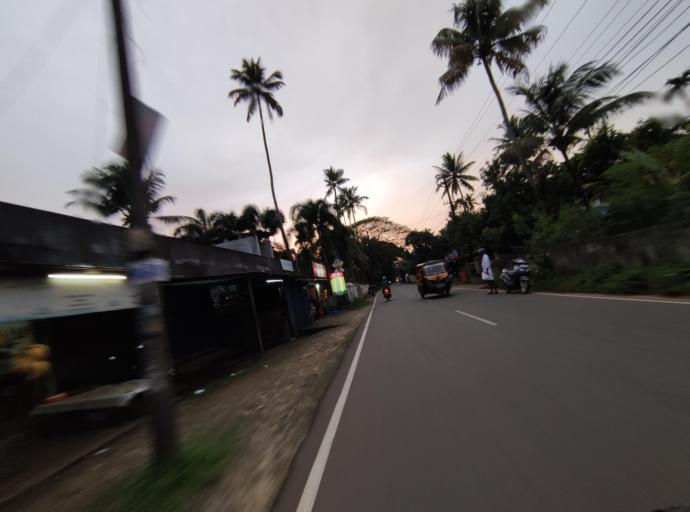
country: IN
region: Kerala
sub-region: Alappuzha
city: Shertallai
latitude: 9.6833
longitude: 76.3561
